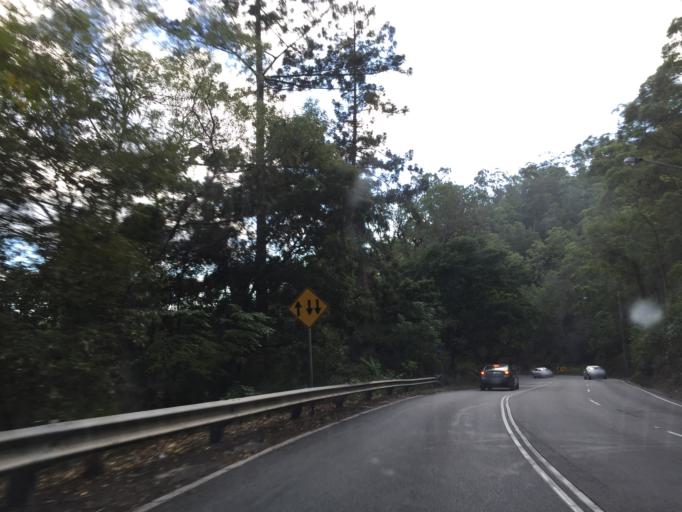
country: AU
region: Queensland
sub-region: Moreton Bay
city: Ferny Hills
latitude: -27.4275
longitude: 152.9442
